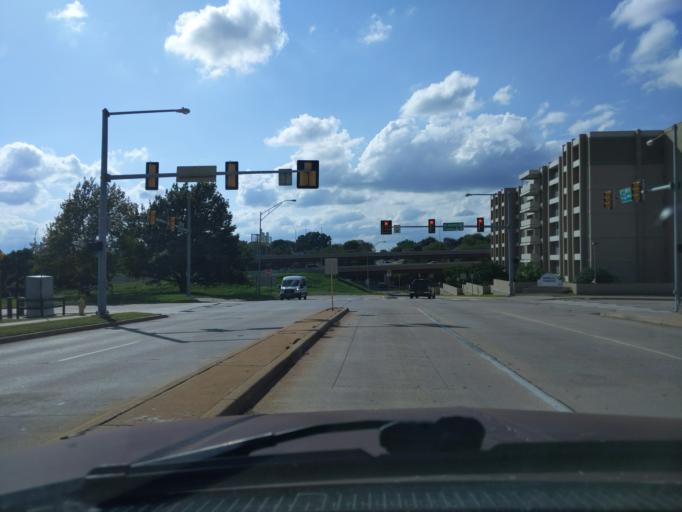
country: US
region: Oklahoma
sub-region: Tulsa County
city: Tulsa
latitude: 36.1479
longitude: -96.0005
